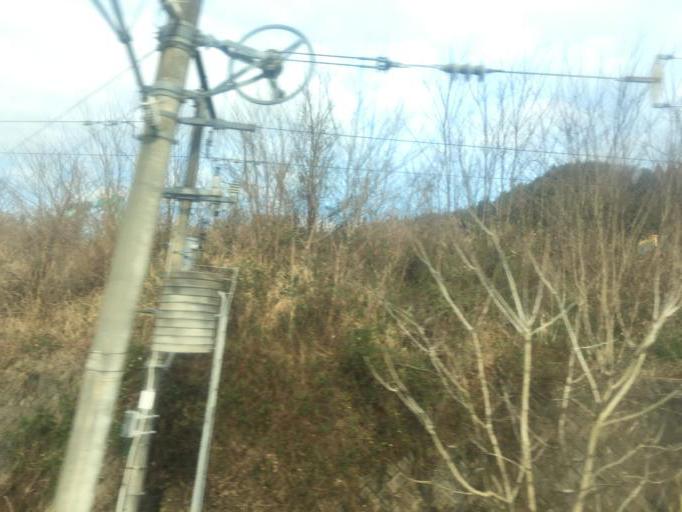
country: JP
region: Akita
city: Takanosu
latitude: 40.2118
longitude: 140.3042
